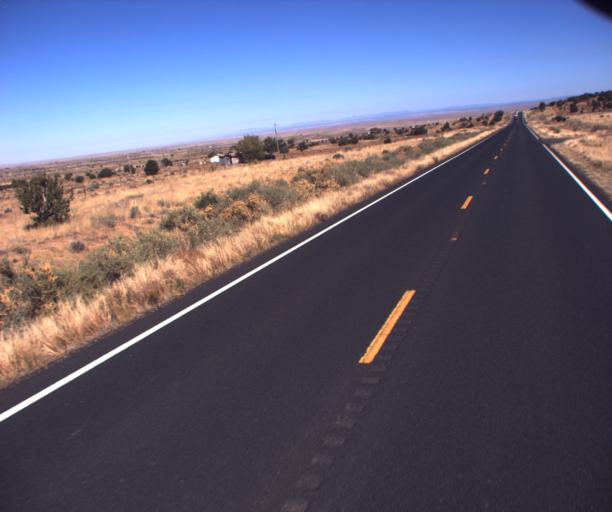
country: US
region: Arizona
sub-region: Apache County
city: Ganado
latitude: 35.7730
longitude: -109.7372
